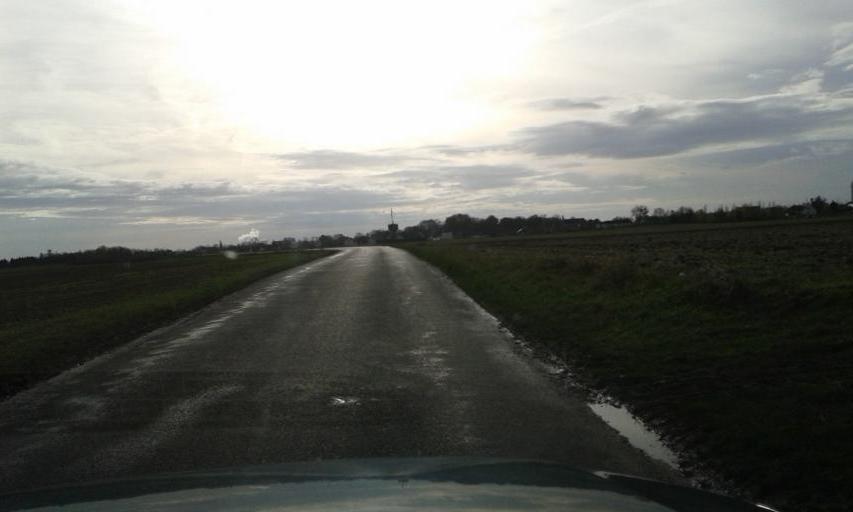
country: FR
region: Centre
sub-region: Departement du Loiret
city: Beaugency
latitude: 47.8035
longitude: 1.6329
